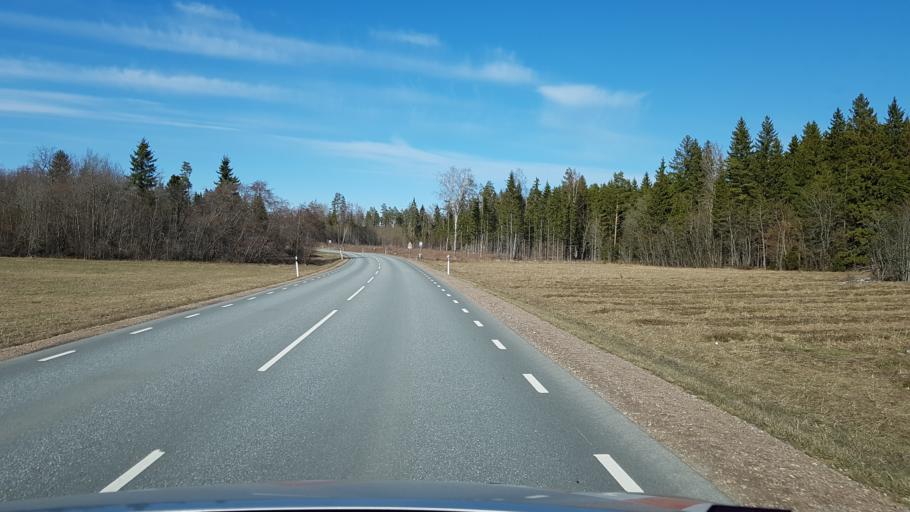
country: EE
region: Laeaene-Virumaa
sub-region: Tapa vald
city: Tapa
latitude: 59.3838
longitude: 26.0154
